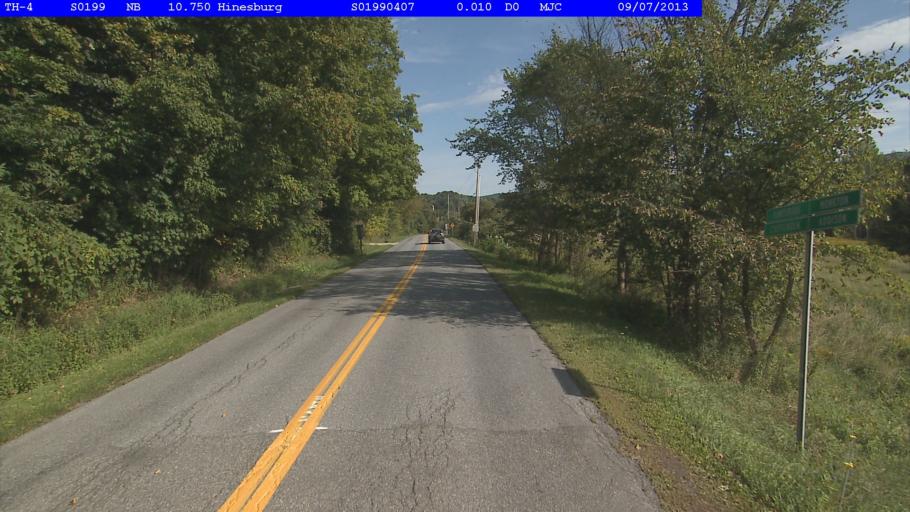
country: US
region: Vermont
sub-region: Chittenden County
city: Hinesburg
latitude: 44.2783
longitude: -73.1096
